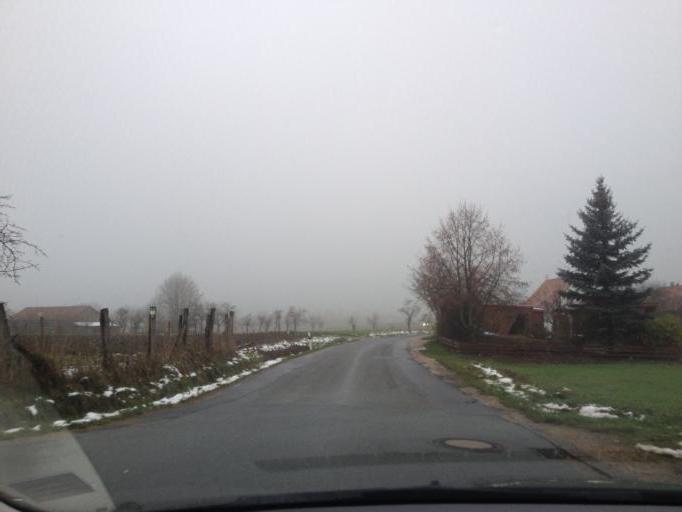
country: DE
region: Bavaria
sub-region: Regierungsbezirk Mittelfranken
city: Heroldsberg
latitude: 49.5466
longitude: 11.2058
